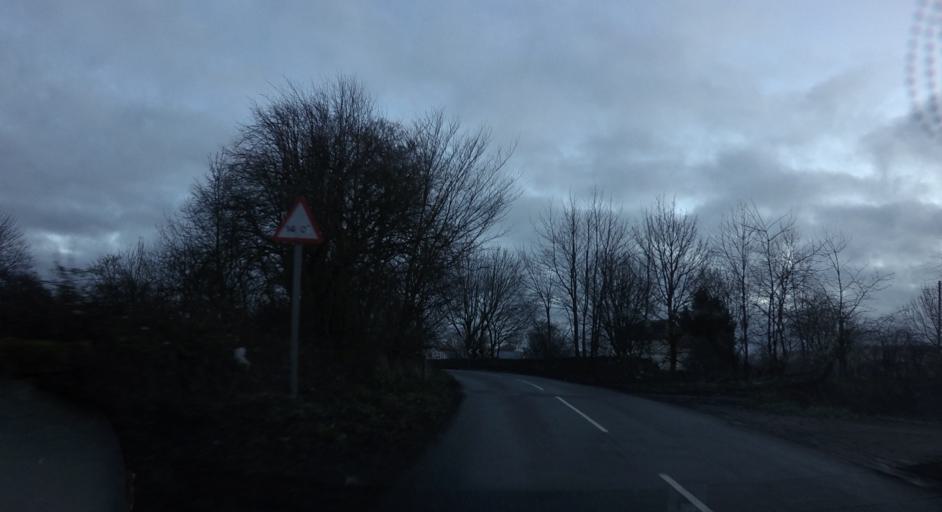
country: GB
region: Scotland
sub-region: Fife
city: Crossford
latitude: 56.0540
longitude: -3.4908
